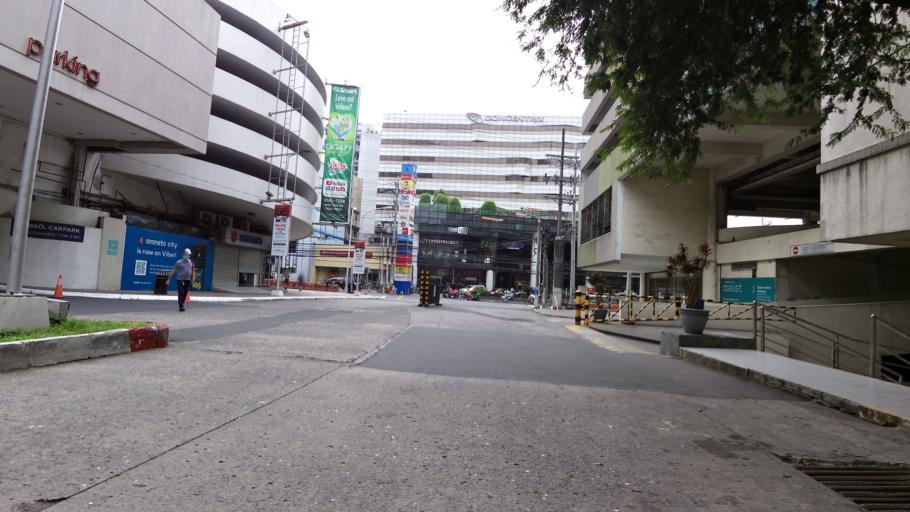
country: PH
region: Metro Manila
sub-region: San Juan
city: San Juan
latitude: 14.6189
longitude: 121.0563
